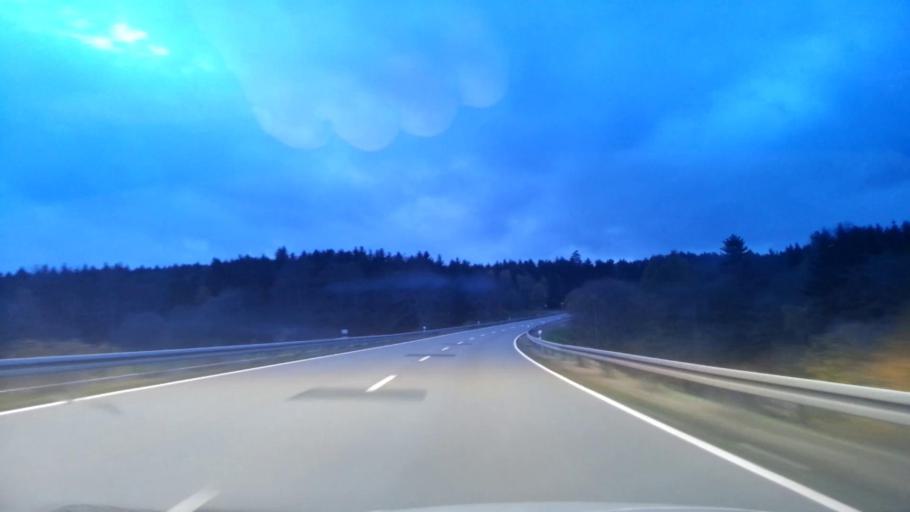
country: DE
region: Bavaria
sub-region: Upper Palatinate
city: Fuchsmuhl
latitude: 49.9304
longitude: 12.1352
